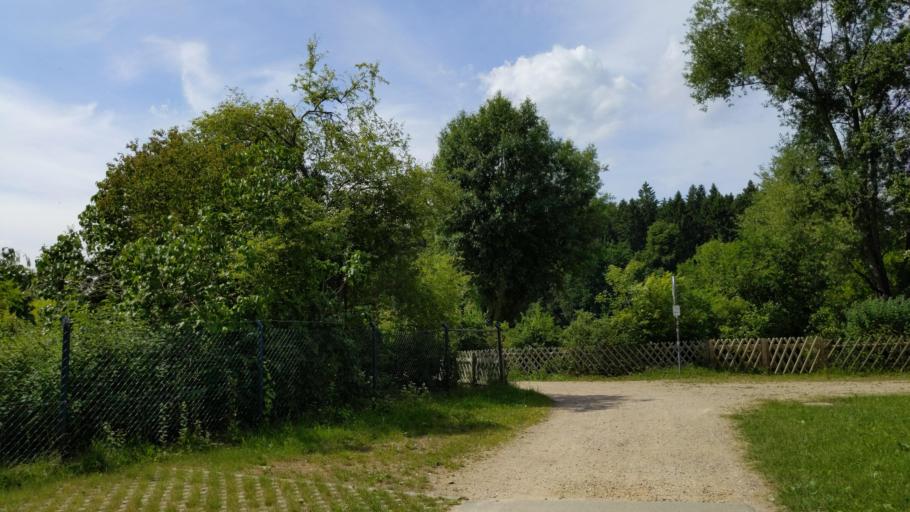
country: DE
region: Schleswig-Holstein
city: Kasseedorf
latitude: 54.1434
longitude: 10.6654
